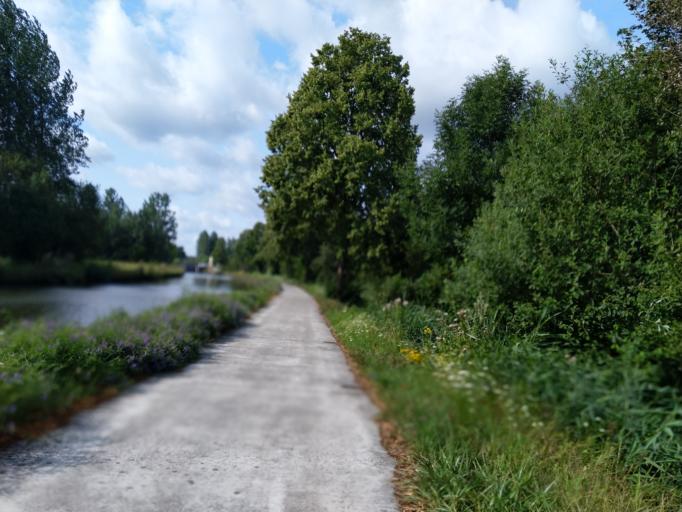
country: BE
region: Wallonia
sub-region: Province du Hainaut
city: Beloeil
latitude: 50.5532
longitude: 3.7481
